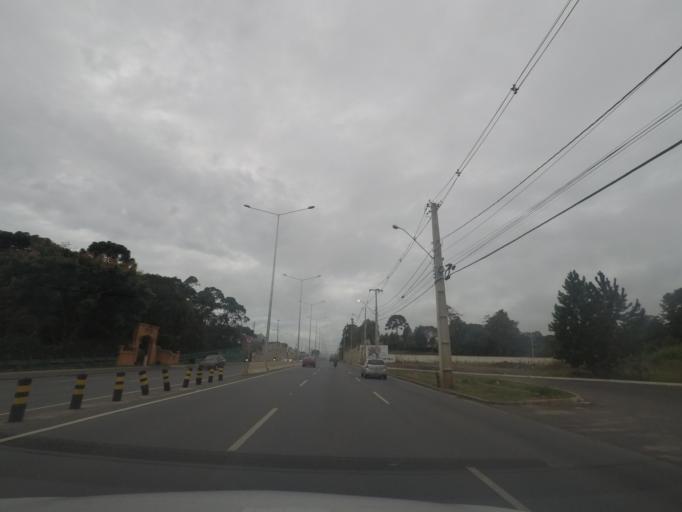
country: BR
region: Parana
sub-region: Piraquara
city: Piraquara
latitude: -25.4560
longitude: -49.1073
